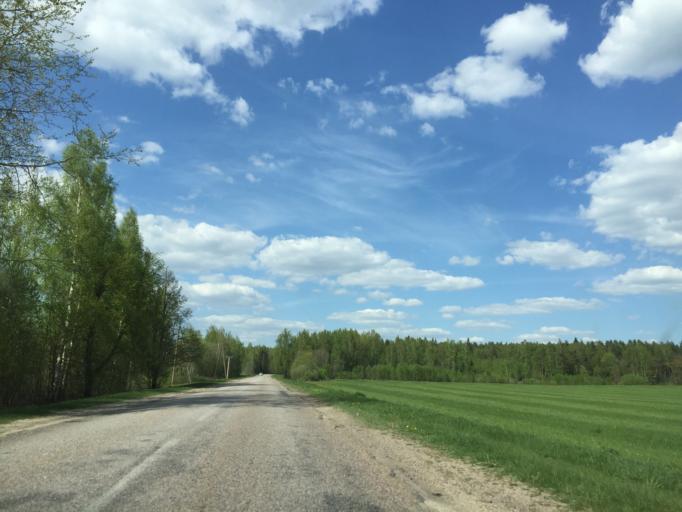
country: LV
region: Limbazu Rajons
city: Limbazi
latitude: 57.4014
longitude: 24.6910
